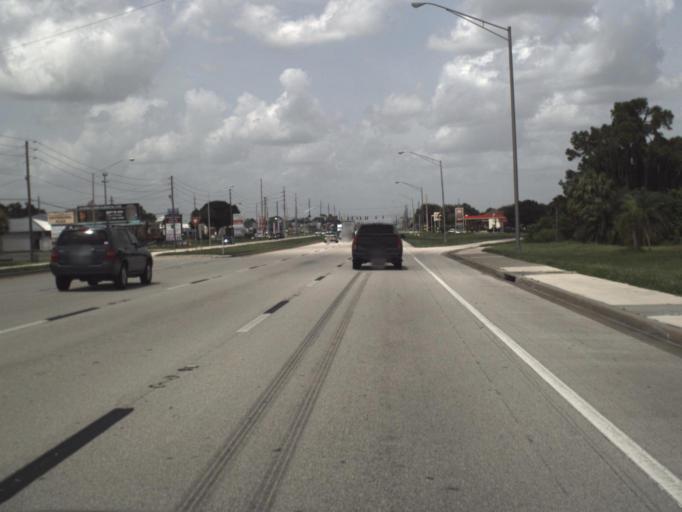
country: US
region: Florida
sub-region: Highlands County
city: Sebring
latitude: 27.4821
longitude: -81.4782
